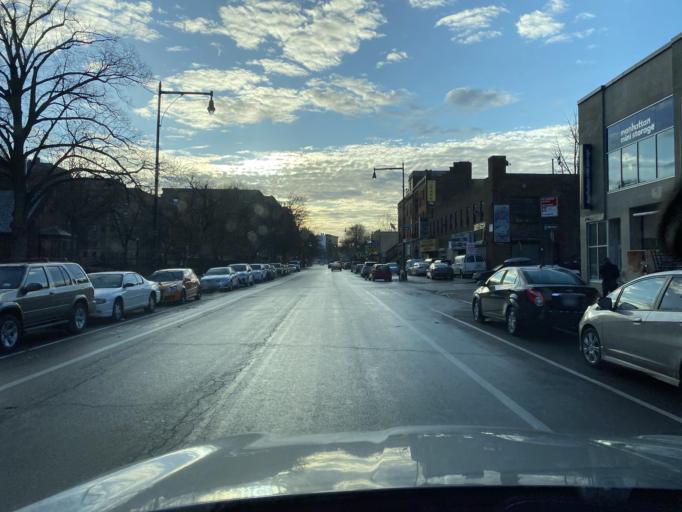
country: US
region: New York
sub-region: New York County
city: Inwood
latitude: 40.8675
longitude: -73.9297
